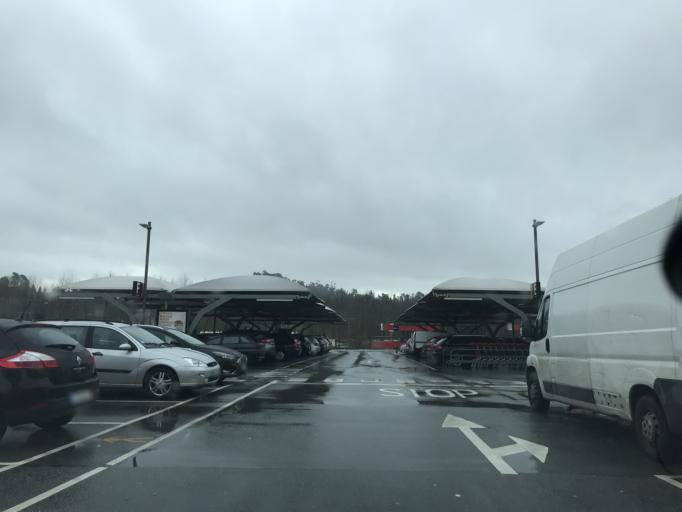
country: PT
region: Braga
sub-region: Vila Nova de Famalicao
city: Vila Nova de Famalicao
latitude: 41.4126
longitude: -8.5129
